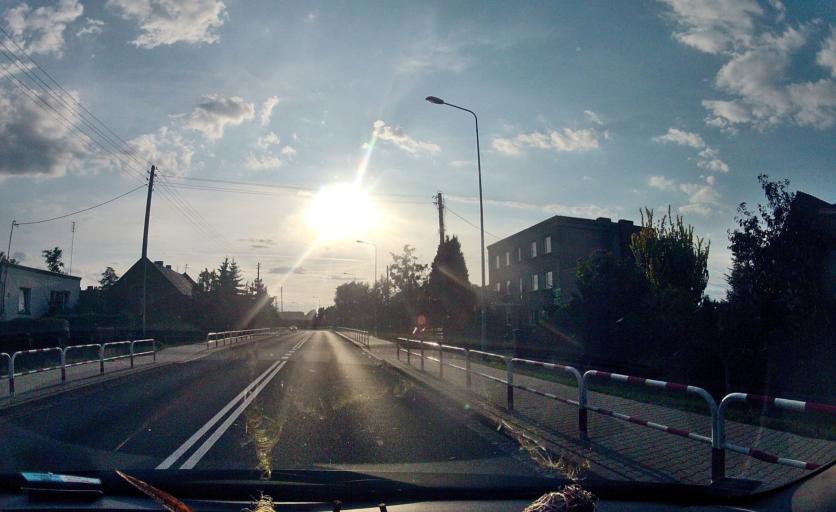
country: PL
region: Opole Voivodeship
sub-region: Powiat kluczborski
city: Kluczbork
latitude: 50.9748
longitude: 18.2317
